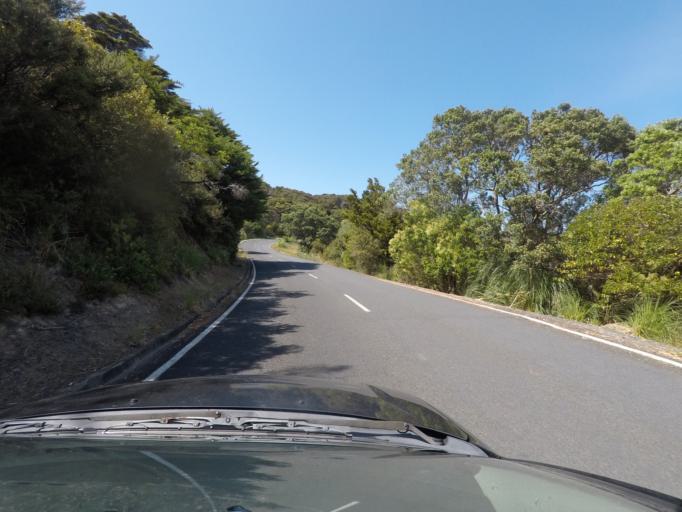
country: NZ
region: Auckland
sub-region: Auckland
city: Warkworth
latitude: -36.3112
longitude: 174.7914
